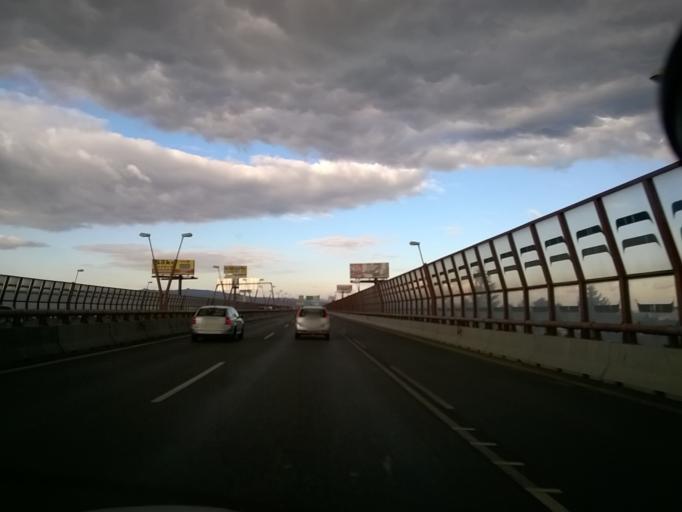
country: SK
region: Bratislavsky
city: Bratislava
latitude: 48.1537
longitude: 17.1816
